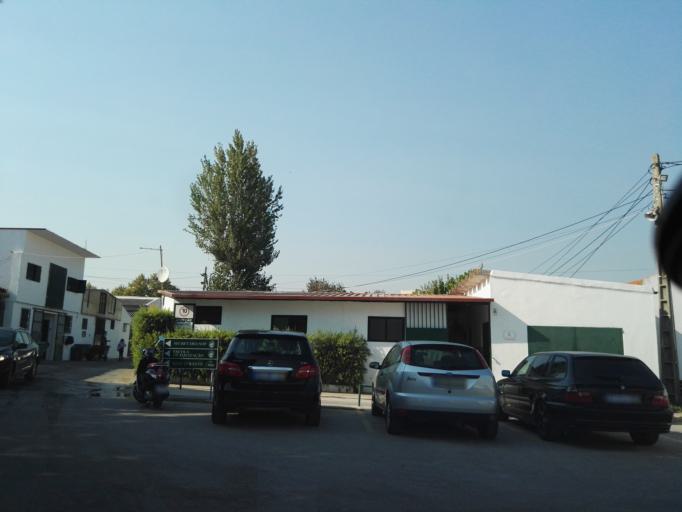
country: PT
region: Lisbon
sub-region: Odivelas
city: Olival do Basto
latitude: 38.7558
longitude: -9.1604
